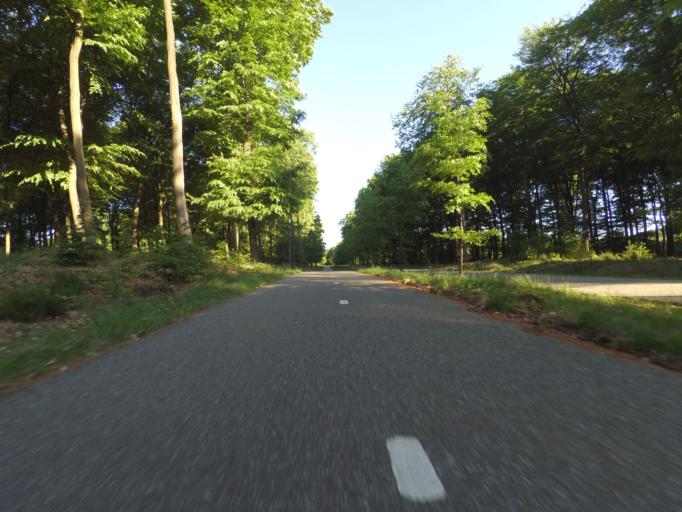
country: NL
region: Gelderland
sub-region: Gemeente Apeldoorn
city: Uddel
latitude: 52.1809
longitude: 5.8534
